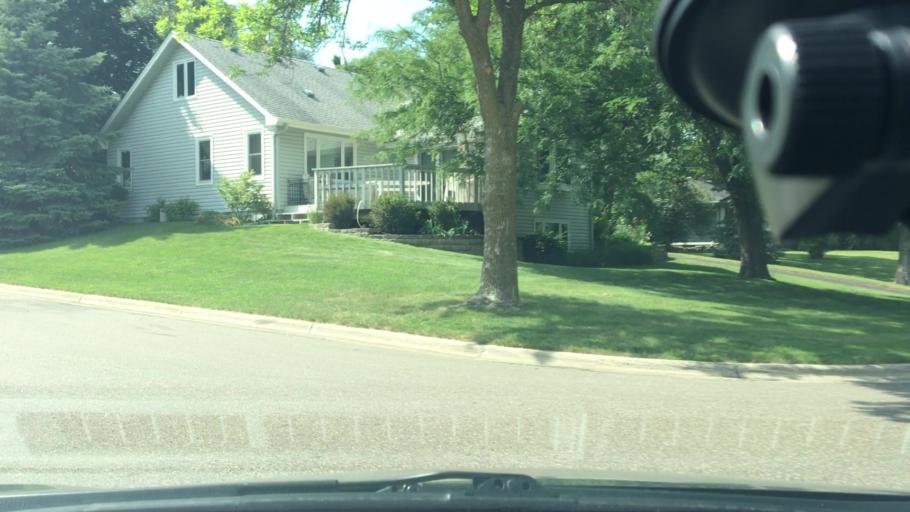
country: US
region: Minnesota
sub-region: Hennepin County
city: New Hope
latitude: 45.0547
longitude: -93.3847
